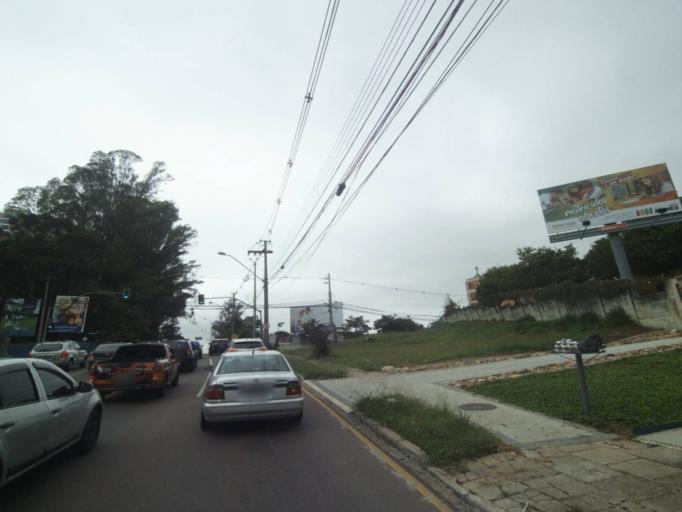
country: BR
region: Parana
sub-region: Curitiba
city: Curitiba
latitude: -25.4388
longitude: -49.3112
